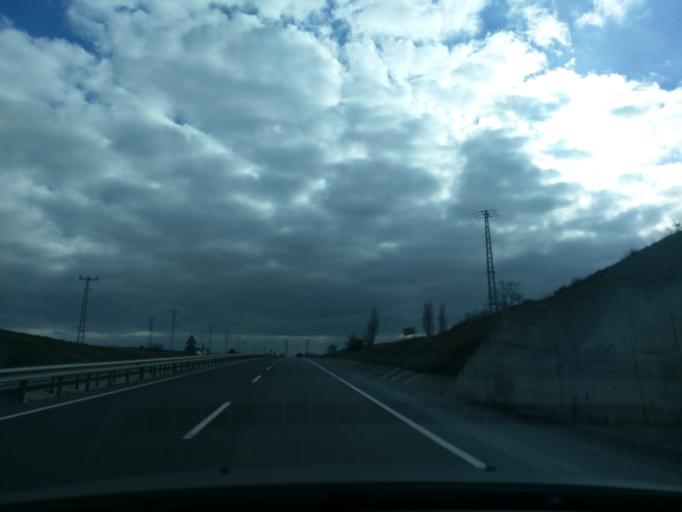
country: TR
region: Istanbul
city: Durusu
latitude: 41.2722
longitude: 28.6657
